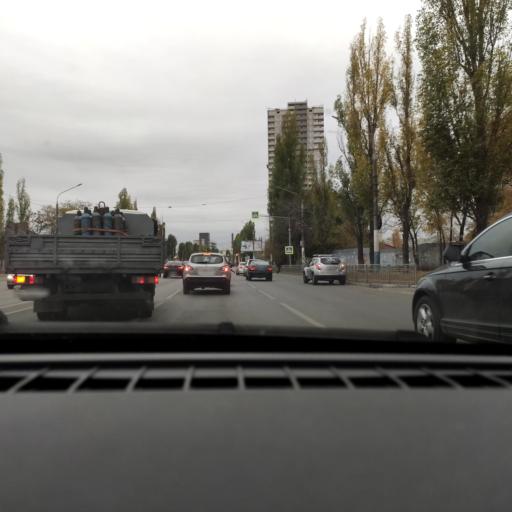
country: RU
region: Voronezj
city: Voronezh
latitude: 51.7052
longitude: 39.2758
